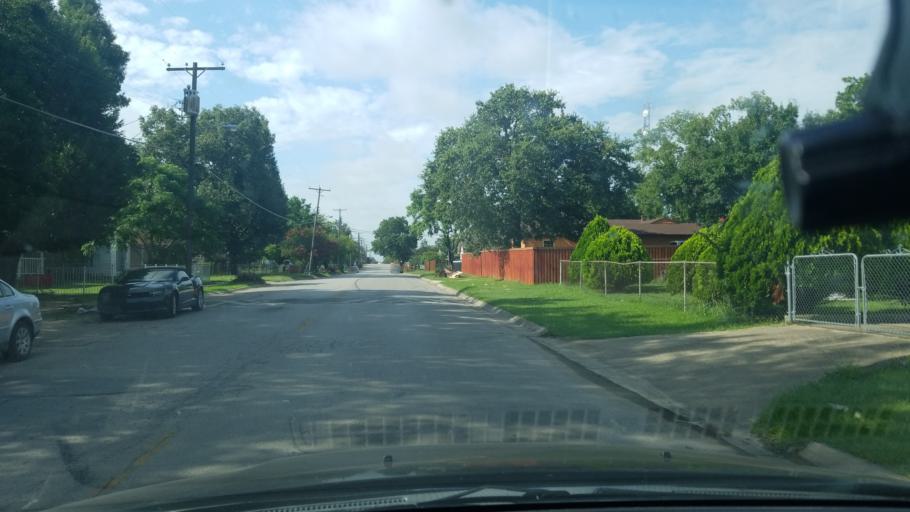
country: US
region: Texas
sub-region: Dallas County
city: Balch Springs
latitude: 32.7373
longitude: -96.6743
